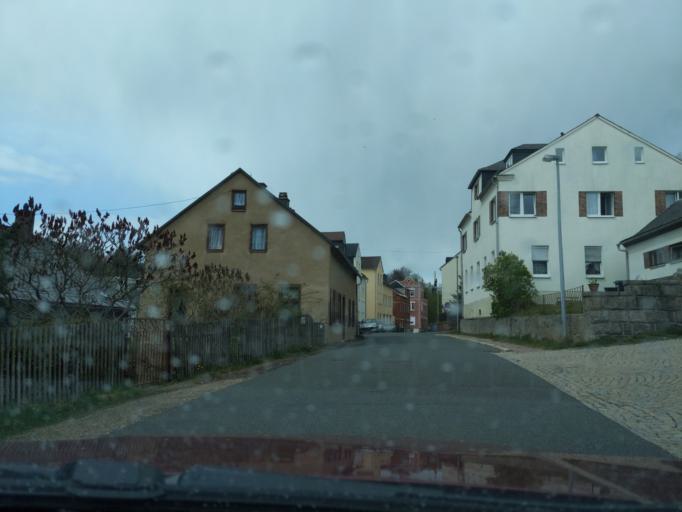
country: DE
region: Saxony
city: Schoenheide
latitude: 50.5038
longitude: 12.5294
